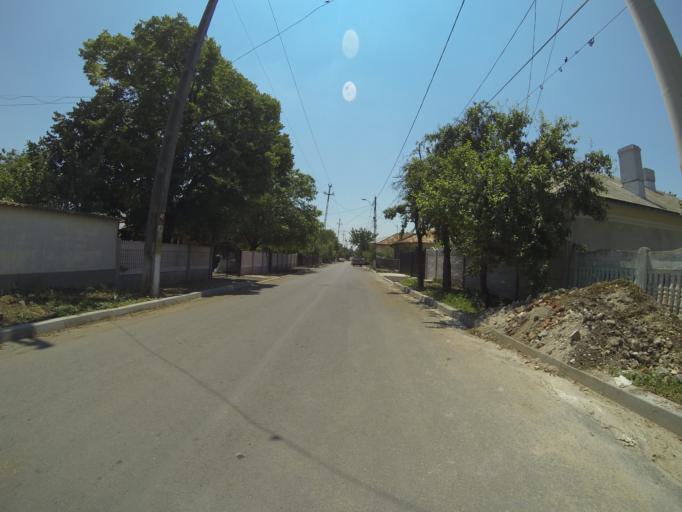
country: RO
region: Dolj
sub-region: Comuna Segarcea
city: Segarcea
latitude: 44.0928
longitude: 23.7518
